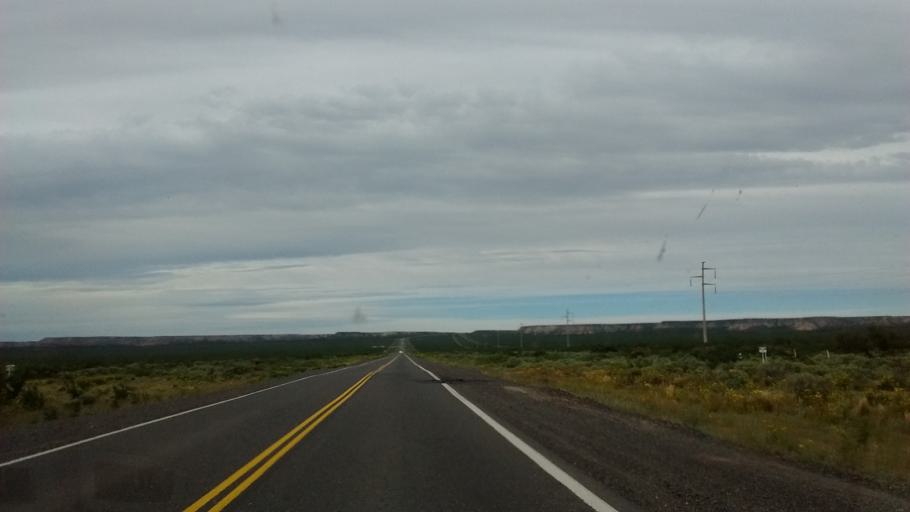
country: AR
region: Rio Negro
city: Catriel
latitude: -38.1570
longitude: -67.9463
